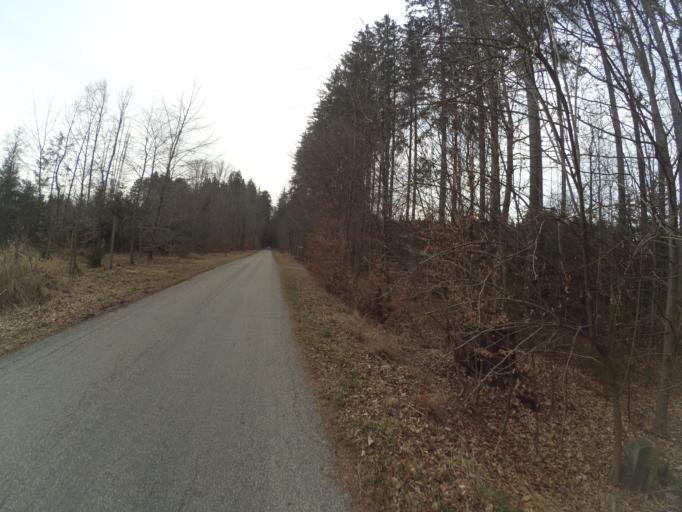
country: DE
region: Bavaria
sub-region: Swabia
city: Bad Worishofen
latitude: 47.9891
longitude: 10.5664
